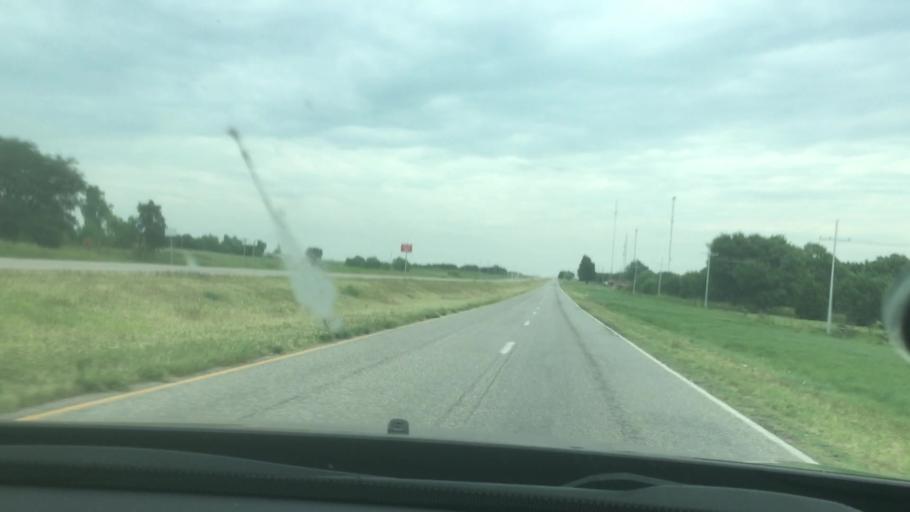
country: US
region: Oklahoma
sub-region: Pontotoc County
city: Ada
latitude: 34.6758
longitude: -96.7743
